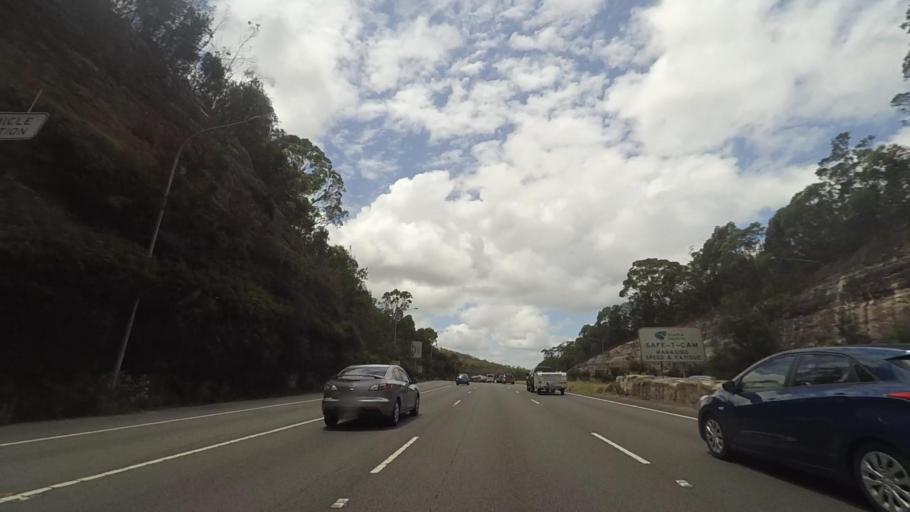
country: AU
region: New South Wales
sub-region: Gosford Shire
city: Point Clare
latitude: -33.4567
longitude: 151.2040
